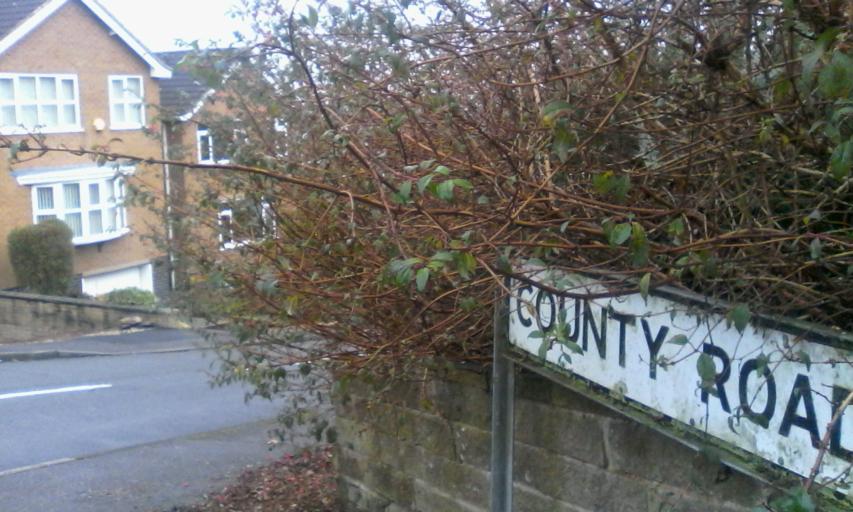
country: GB
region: England
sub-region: Nottinghamshire
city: Arnold
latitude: 52.9820
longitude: -1.1028
